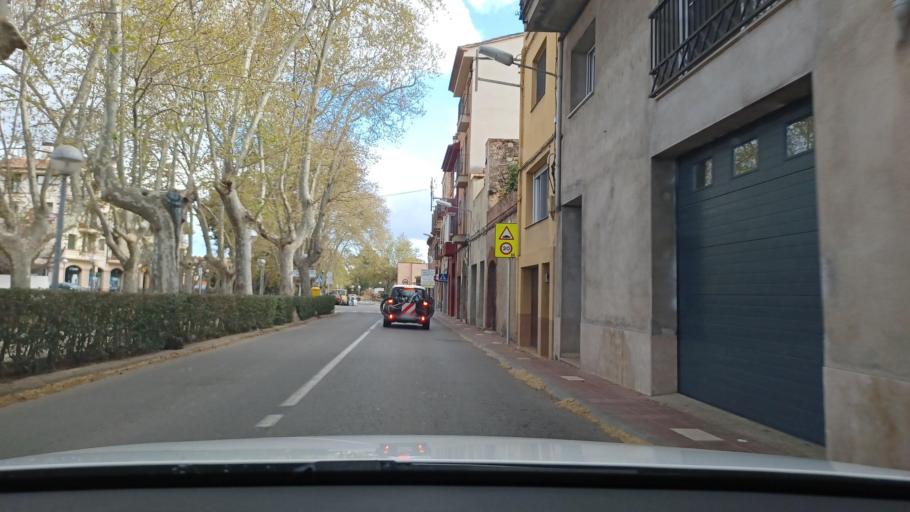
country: ES
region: Catalonia
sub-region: Provincia de Tarragona
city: Botarell
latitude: 41.1214
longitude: 1.0037
